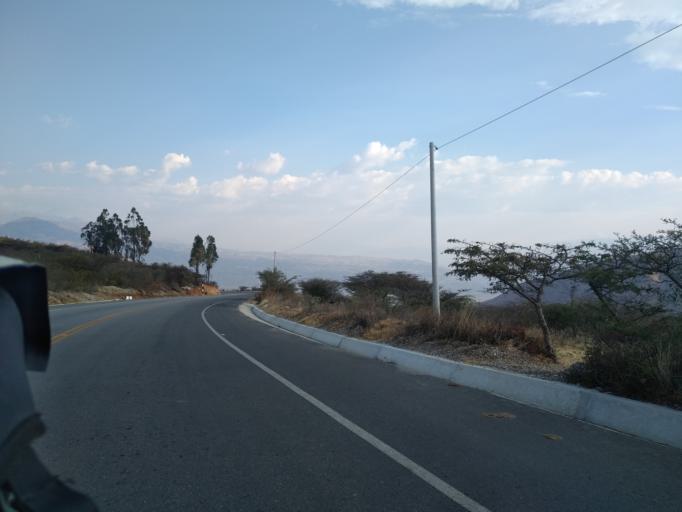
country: PE
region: Cajamarca
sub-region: San Marcos
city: La Grama
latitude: -7.4029
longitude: -78.1246
